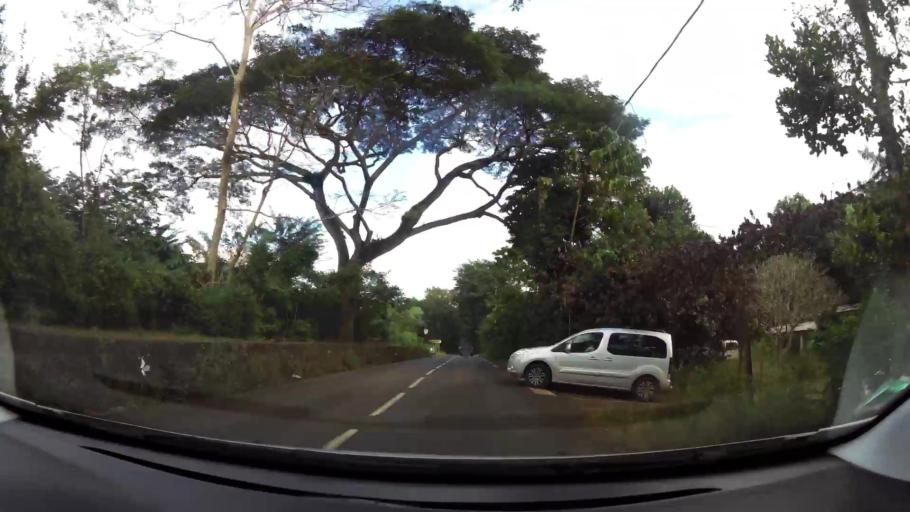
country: YT
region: Ouangani
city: Ouangani
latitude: -12.8339
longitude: 45.1358
